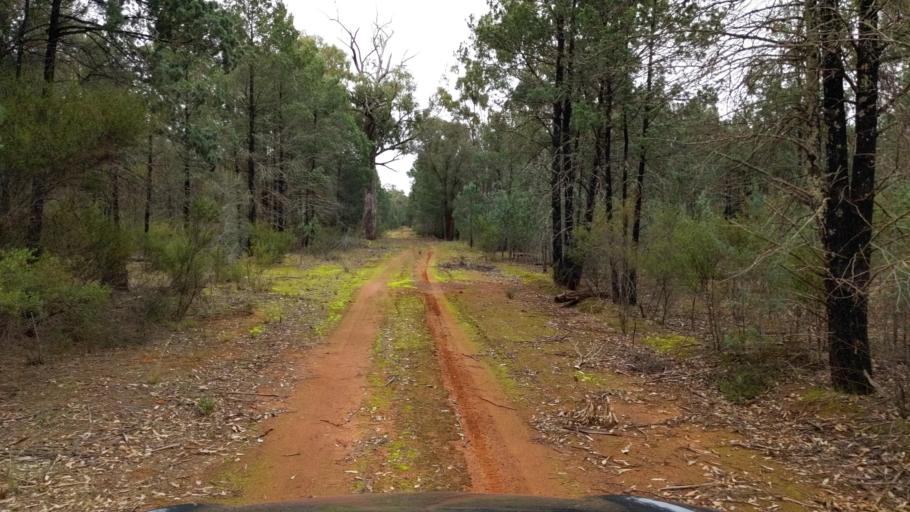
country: AU
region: New South Wales
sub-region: Coolamon
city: Coolamon
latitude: -34.8459
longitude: 146.9328
